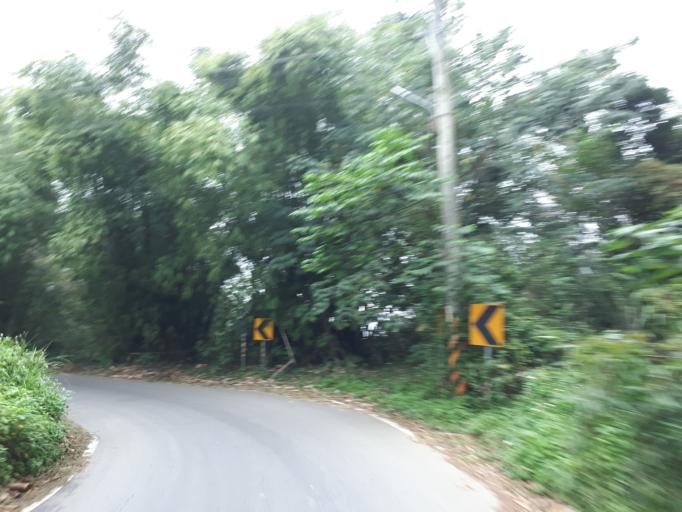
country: TW
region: Taiwan
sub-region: Hsinchu
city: Zhubei
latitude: 24.7348
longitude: 121.0774
